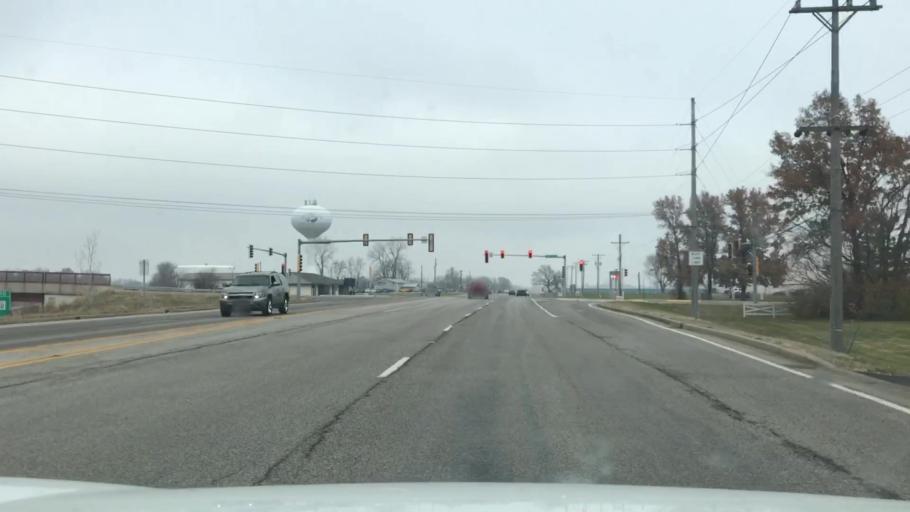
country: US
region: Illinois
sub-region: Madison County
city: Rosewood Heights
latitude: 38.8867
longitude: -90.0590
